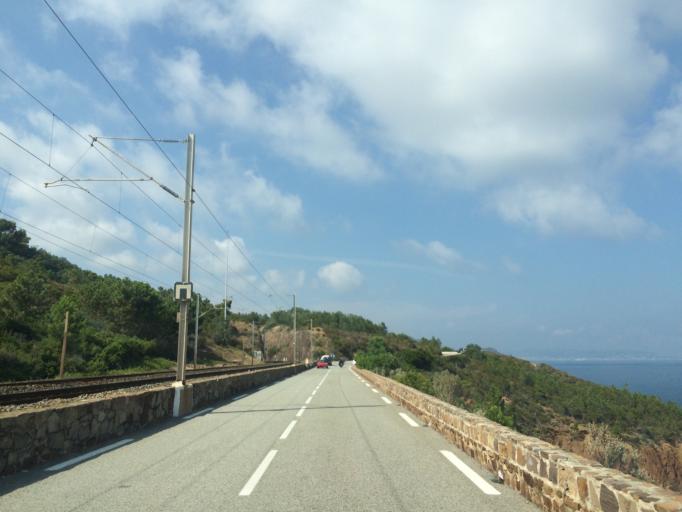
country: FR
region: Provence-Alpes-Cote d'Azur
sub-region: Departement des Alpes-Maritimes
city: Theoule-sur-Mer
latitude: 43.4528
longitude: 6.9199
